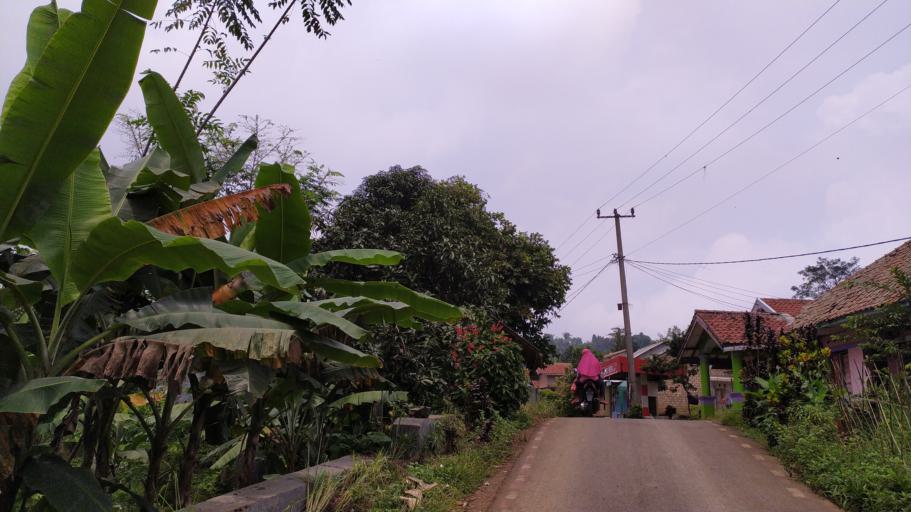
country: ID
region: West Java
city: Ciampea
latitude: -6.6288
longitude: 106.7133
